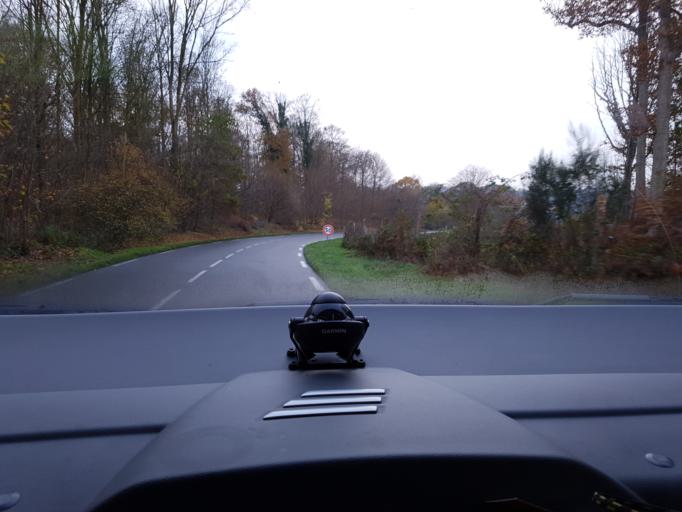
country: FR
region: Haute-Normandie
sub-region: Departement de la Seine-Maritime
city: Duclair
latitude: 49.4902
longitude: 0.8902
